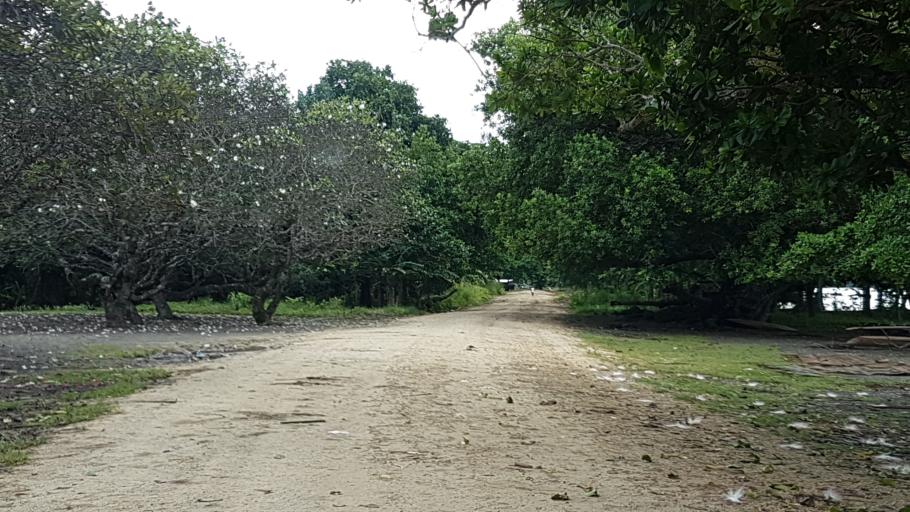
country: PG
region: Milne Bay
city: Alotau
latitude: -10.2894
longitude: 150.7675
